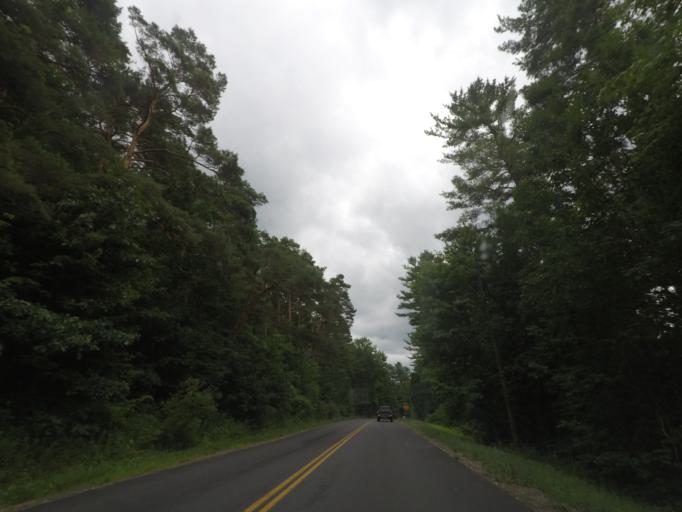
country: US
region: New York
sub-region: Rensselaer County
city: Poestenkill
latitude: 42.8230
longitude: -73.5161
